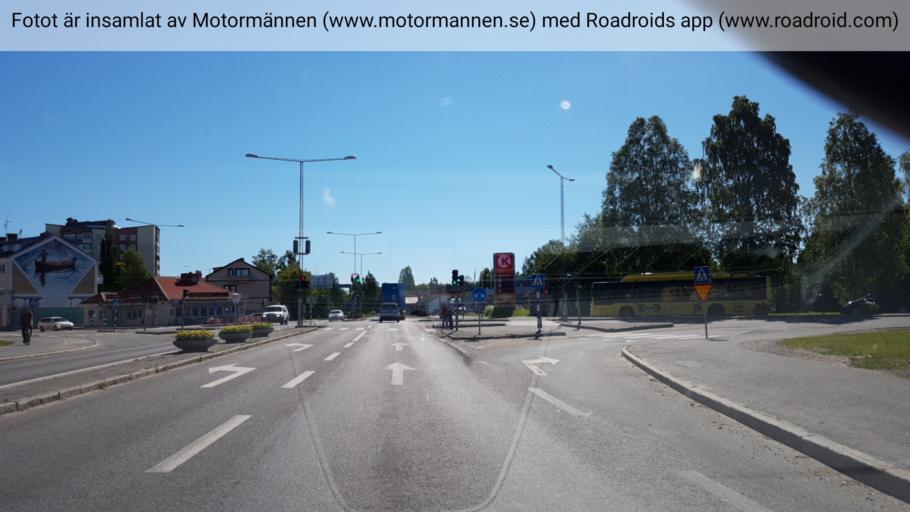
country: SE
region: Norrbotten
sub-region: Bodens Kommun
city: Boden
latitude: 65.8221
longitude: 21.6783
